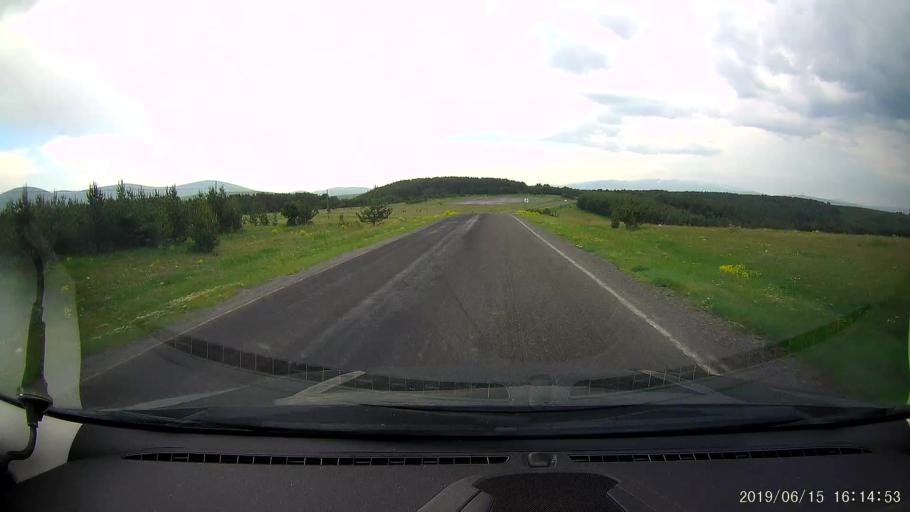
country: TR
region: Ardahan
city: Hanak
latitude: 41.2745
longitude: 42.8501
